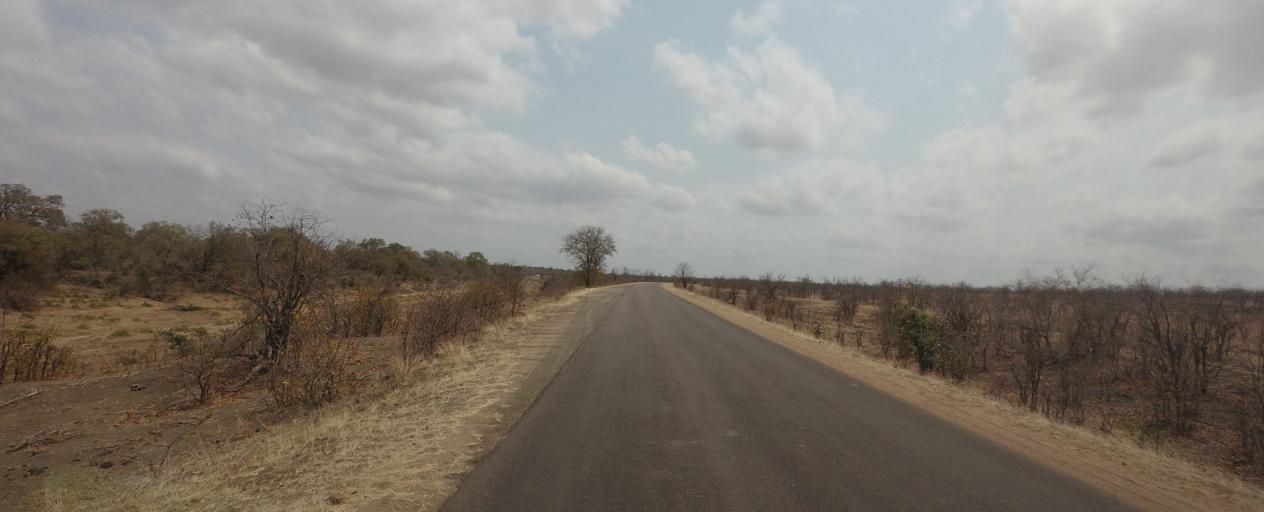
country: ZA
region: Limpopo
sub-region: Mopani District Municipality
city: Phalaborwa
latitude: -23.5895
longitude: 31.4520
